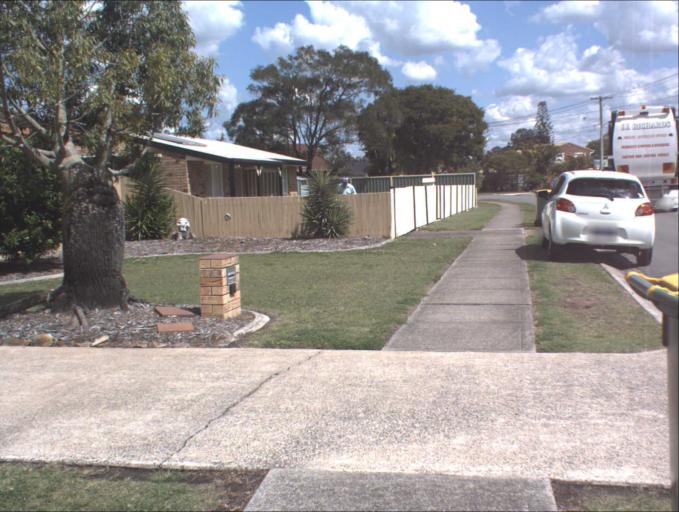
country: AU
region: Queensland
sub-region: Logan
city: Waterford West
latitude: -27.6807
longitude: 153.1483
